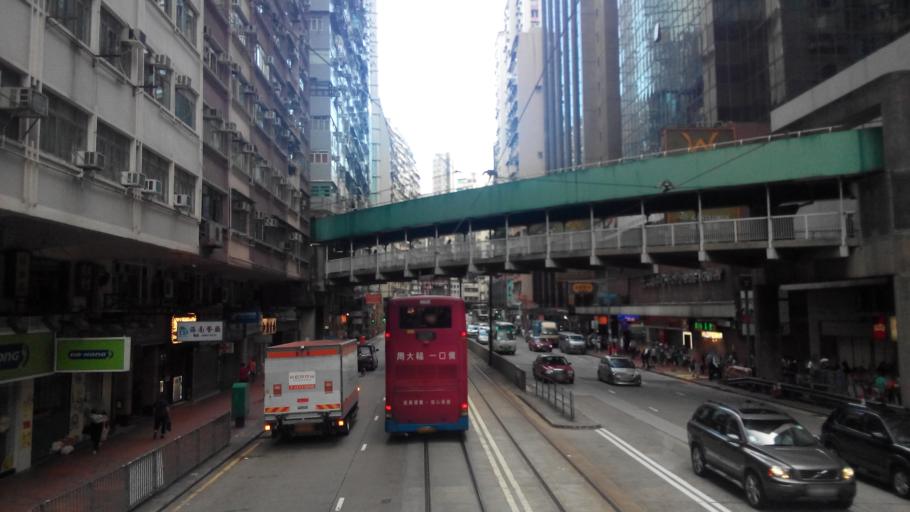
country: HK
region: Wanchai
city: Wan Chai
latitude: 22.2884
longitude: 114.1938
